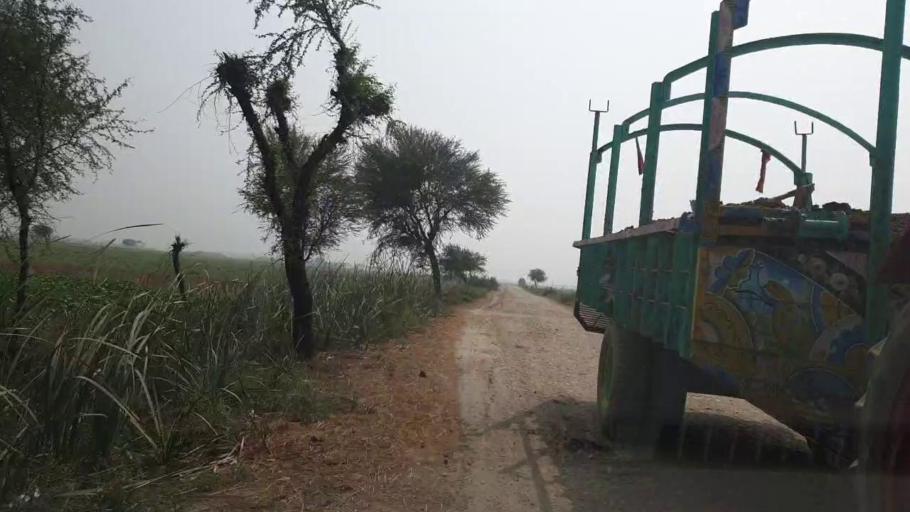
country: PK
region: Sindh
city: Kario
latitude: 24.6527
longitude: 68.5957
